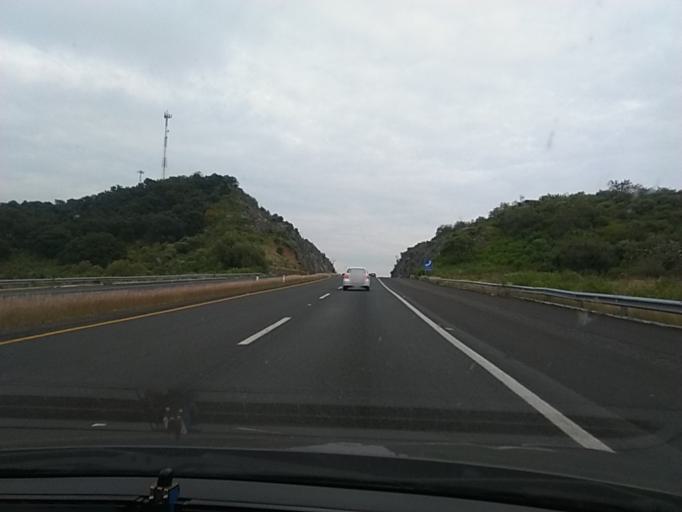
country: MX
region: Michoacan
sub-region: Puruandiro
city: San Lorenzo
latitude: 19.9430
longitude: -101.6311
